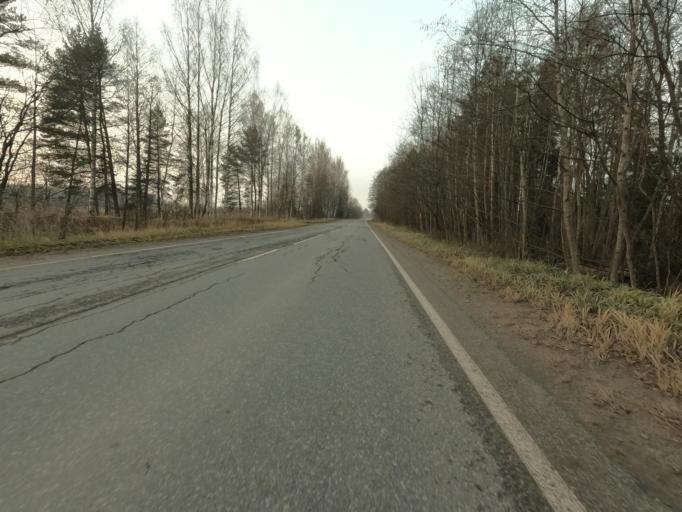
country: RU
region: Leningrad
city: Kirovsk
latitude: 59.8254
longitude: 30.9821
